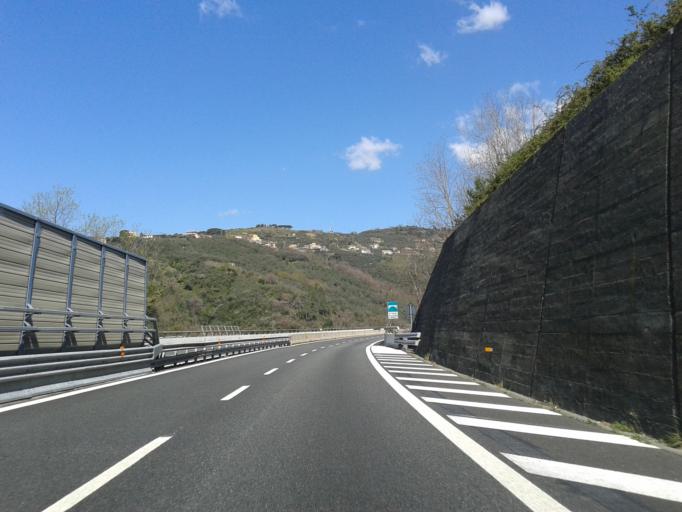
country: IT
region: Liguria
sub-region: Provincia di Genova
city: Sestri Levante
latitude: 44.2941
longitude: 9.3845
